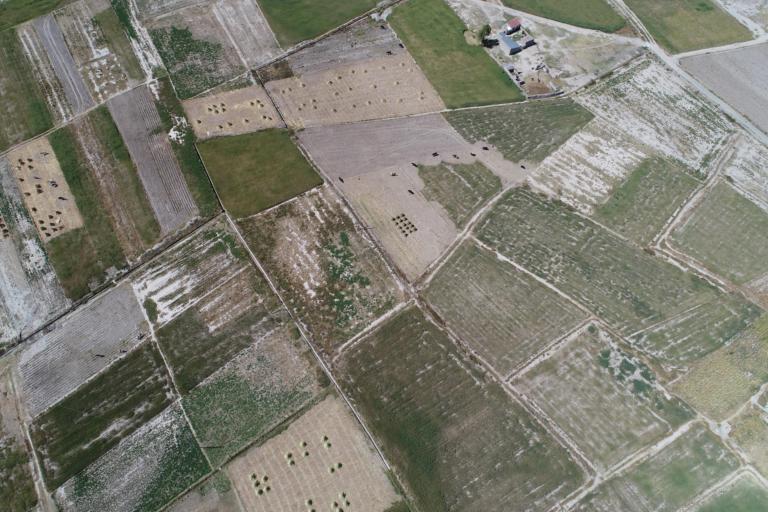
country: BO
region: La Paz
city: Achacachi
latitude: -16.0192
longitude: -68.7184
